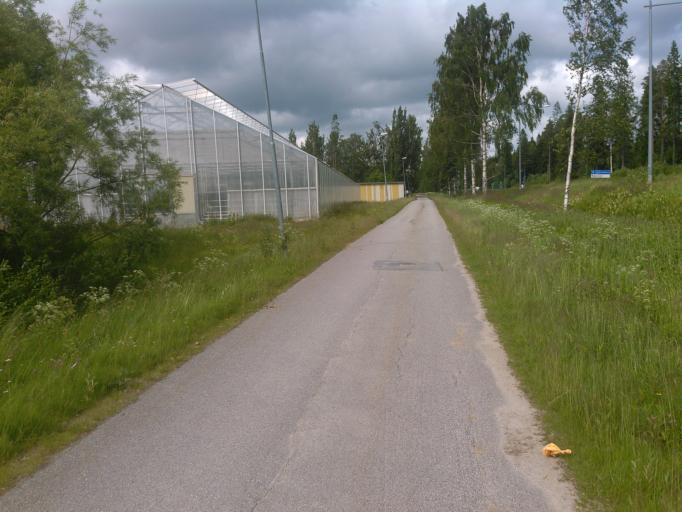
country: SE
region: Vaesterbotten
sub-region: Umea Kommun
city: Roback
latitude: 63.8631
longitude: 20.1993
